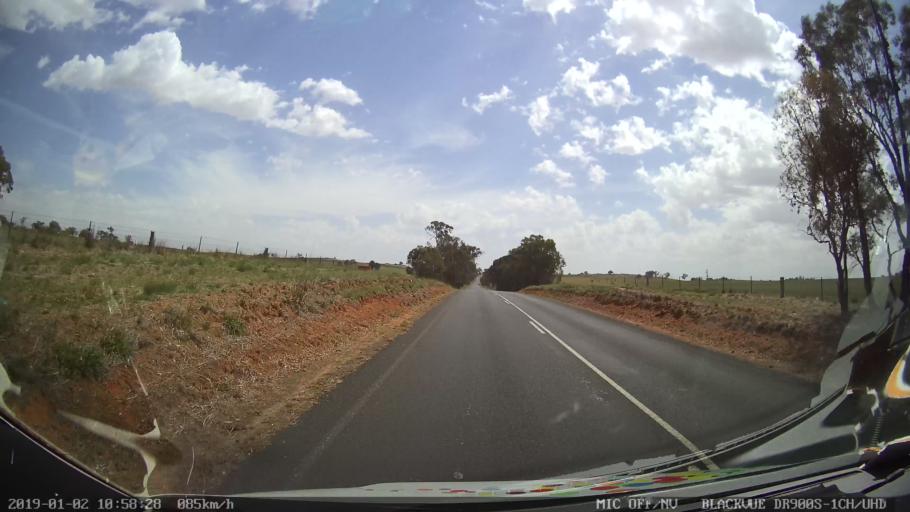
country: AU
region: New South Wales
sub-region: Cootamundra
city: Cootamundra
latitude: -34.6242
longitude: 148.2916
